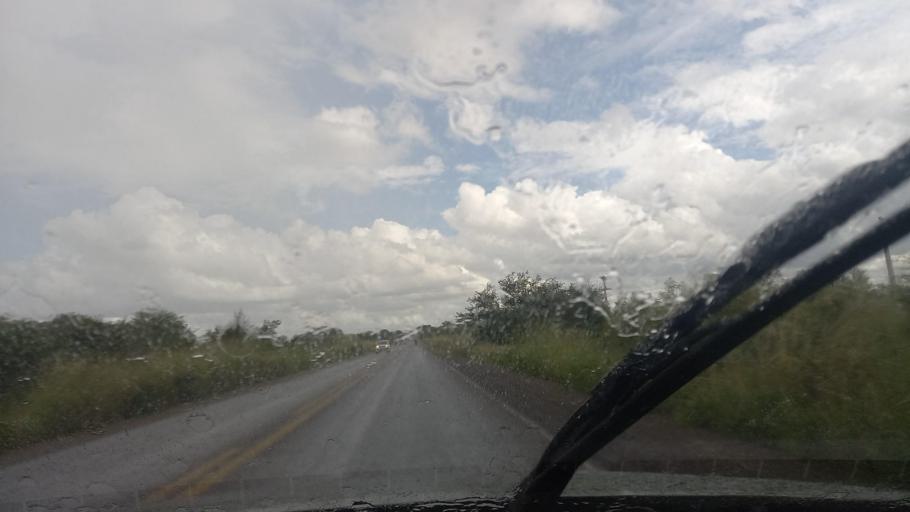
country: BR
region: Pernambuco
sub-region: Cachoeirinha
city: Cachoeirinha
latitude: -8.5543
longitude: -36.2739
